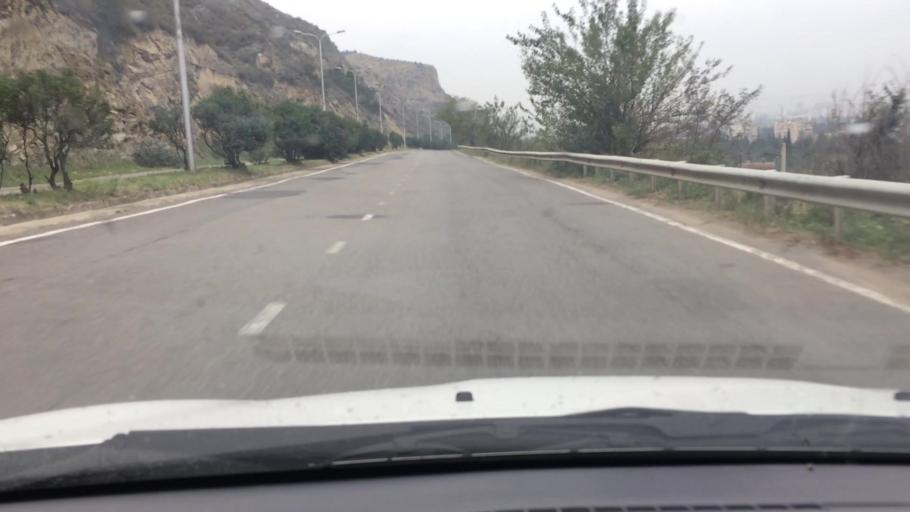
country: GE
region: T'bilisi
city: Tbilisi
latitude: 41.6536
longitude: 44.9005
